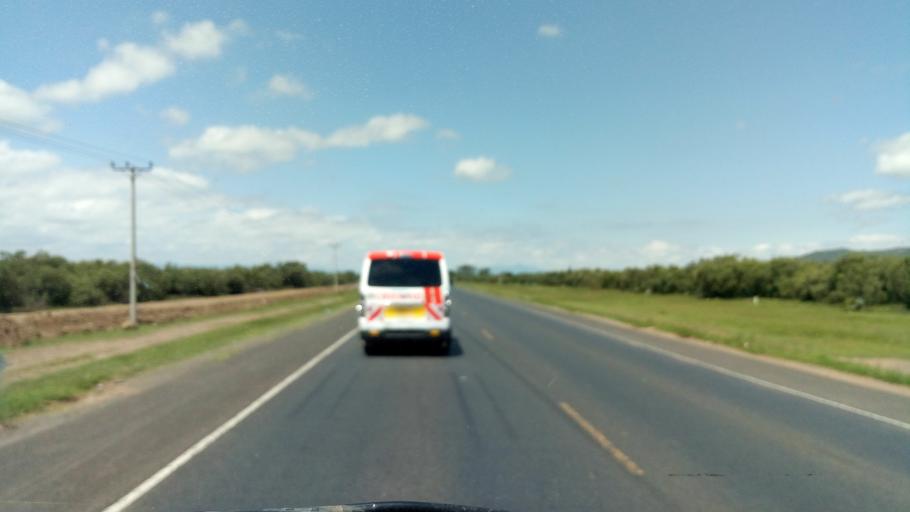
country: KE
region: Nakuru
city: Naivasha
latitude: -0.5565
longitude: 36.3508
